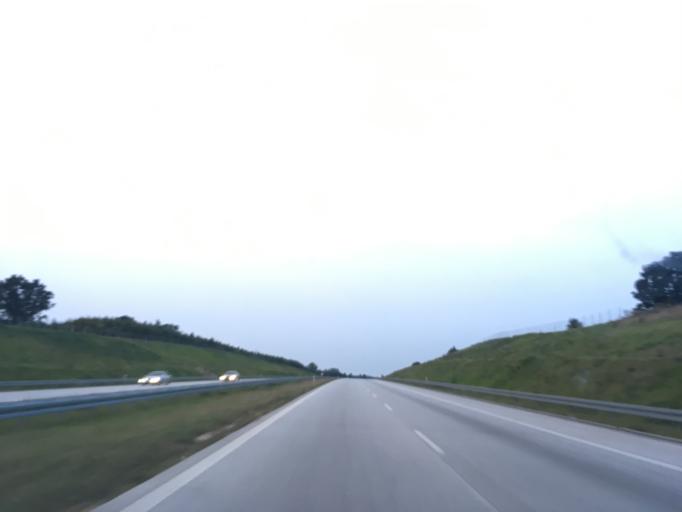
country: PL
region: Lodz Voivodeship
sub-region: Powiat zgierski
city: Strykow
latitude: 51.8325
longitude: 19.6553
